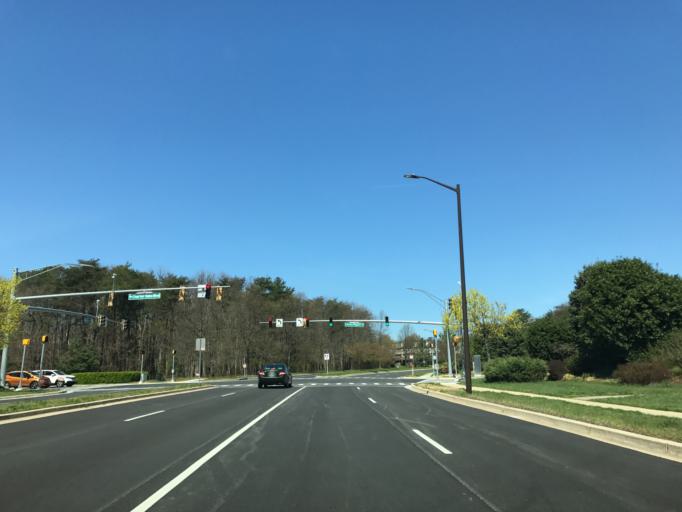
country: US
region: Maryland
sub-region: Anne Arundel County
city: Odenton
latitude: 39.1079
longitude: -76.7122
